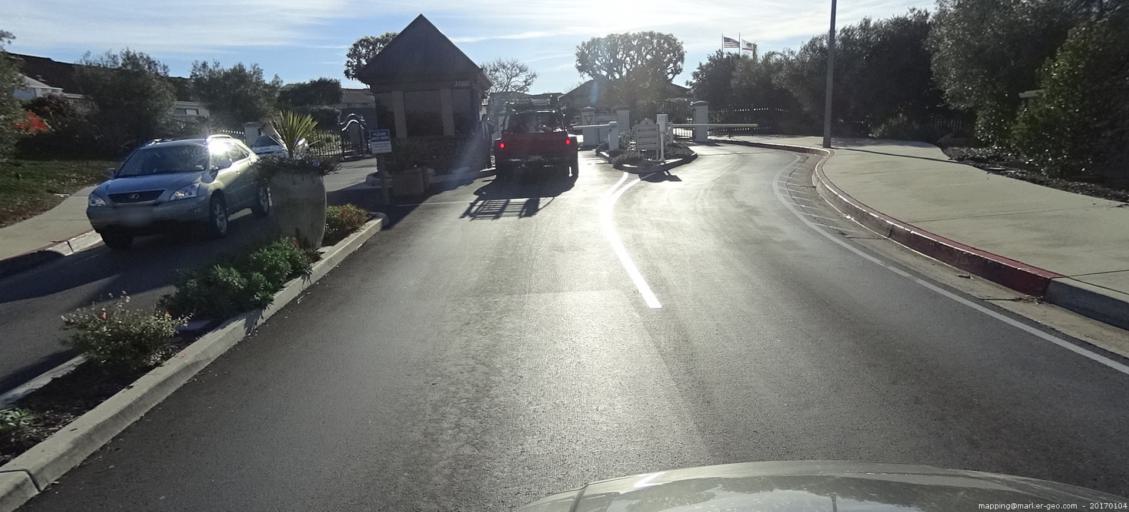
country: US
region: California
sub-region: Orange County
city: Dana Point
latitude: 33.4761
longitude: -117.7141
